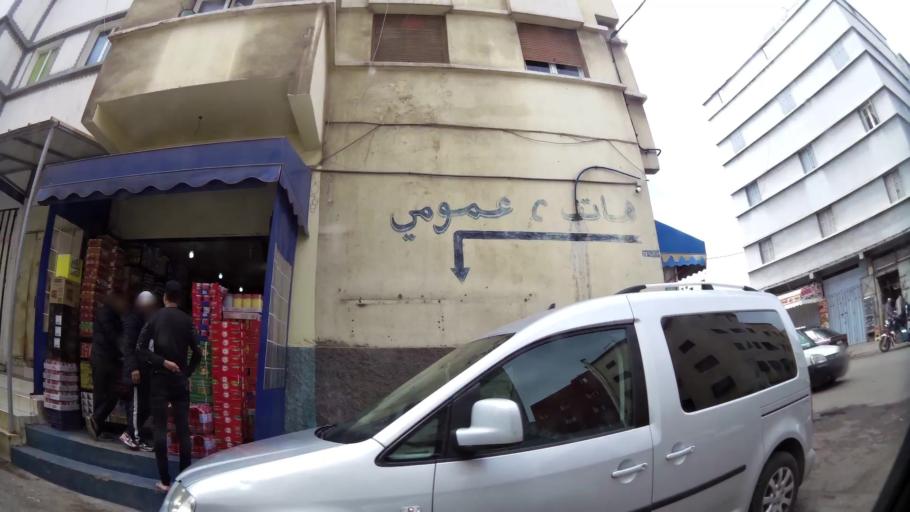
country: MA
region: Grand Casablanca
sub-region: Mediouna
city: Tit Mellil
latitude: 33.6061
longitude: -7.5145
